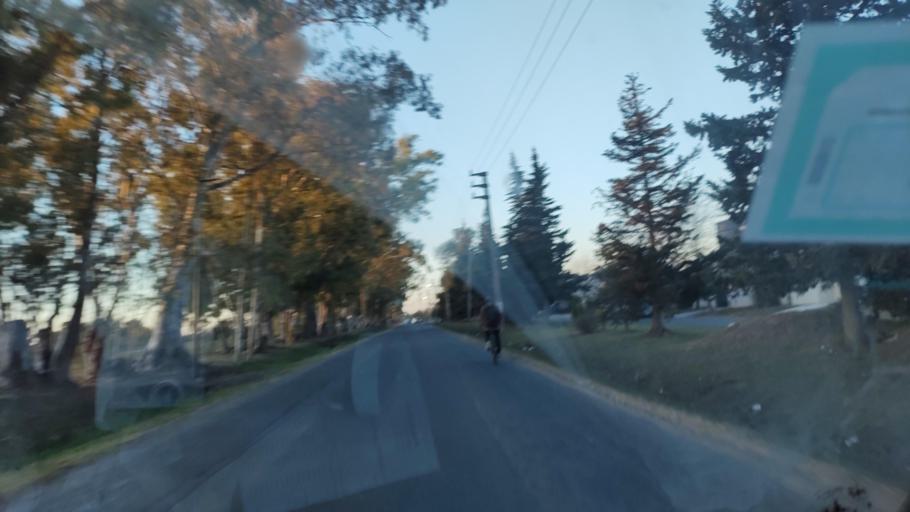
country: AR
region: Buenos Aires
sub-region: Partido de La Plata
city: La Plata
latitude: -34.9039
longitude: -58.0313
